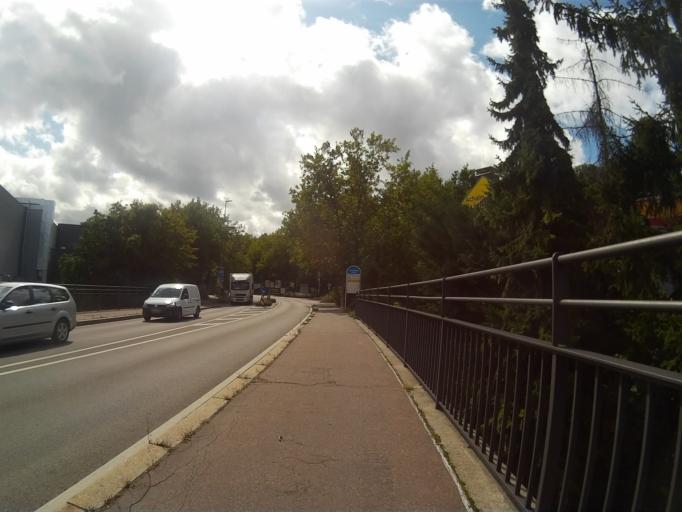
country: DE
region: Baden-Wuerttemberg
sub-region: Tuebingen Region
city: Pfullingen
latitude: 48.4757
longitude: 9.2203
